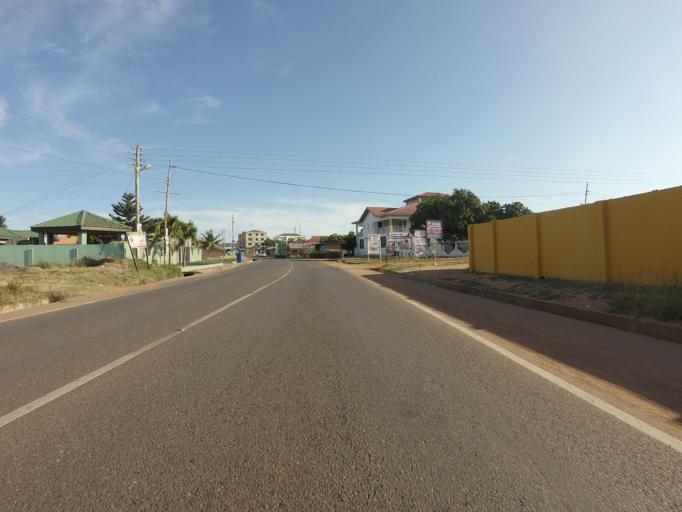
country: GH
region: Greater Accra
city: Nungua
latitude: 5.6391
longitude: -0.0925
